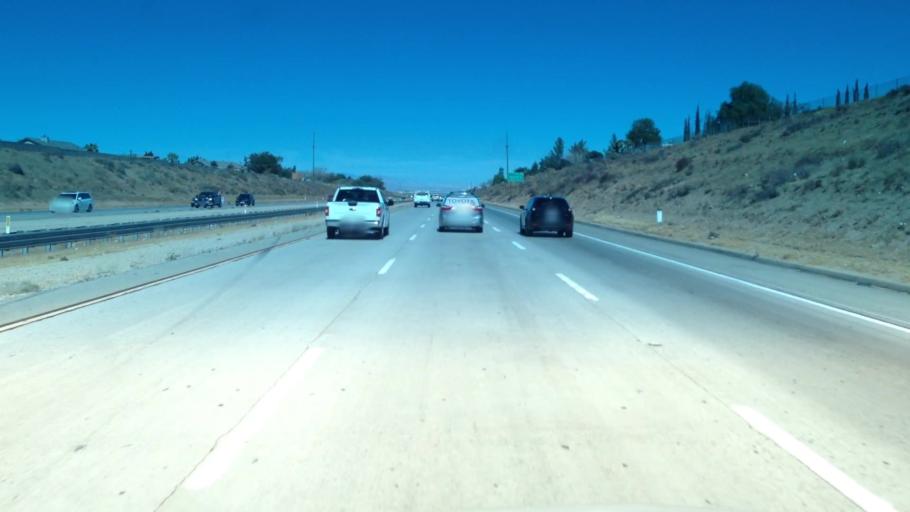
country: US
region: California
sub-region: Los Angeles County
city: Desert View Highlands
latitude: 34.6204
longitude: -118.1530
